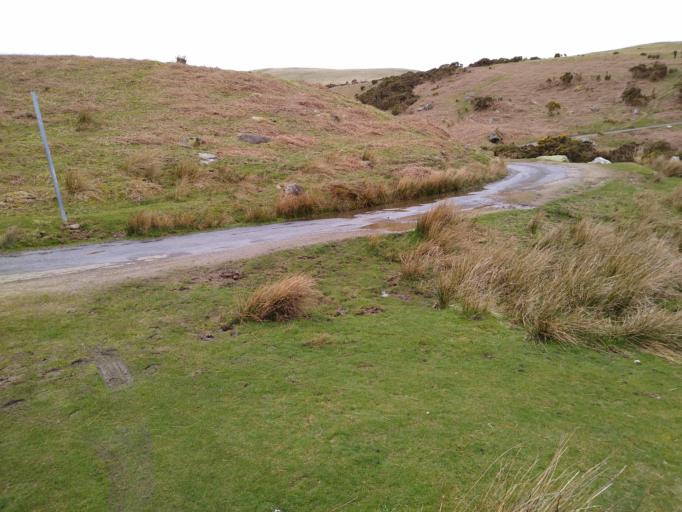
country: GB
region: England
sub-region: Cumbria
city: Keswick
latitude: 54.7058
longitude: -3.0099
